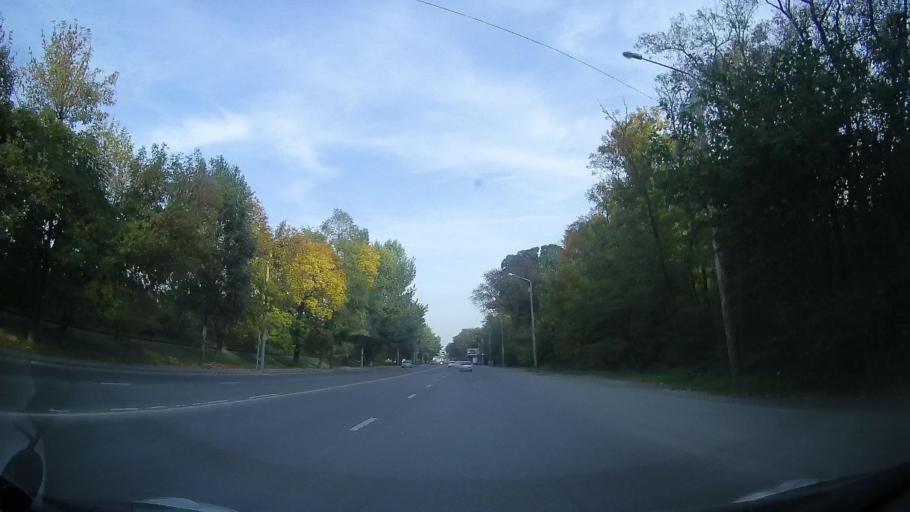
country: RU
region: Rostov
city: Aksay
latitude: 47.2752
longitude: 39.8118
